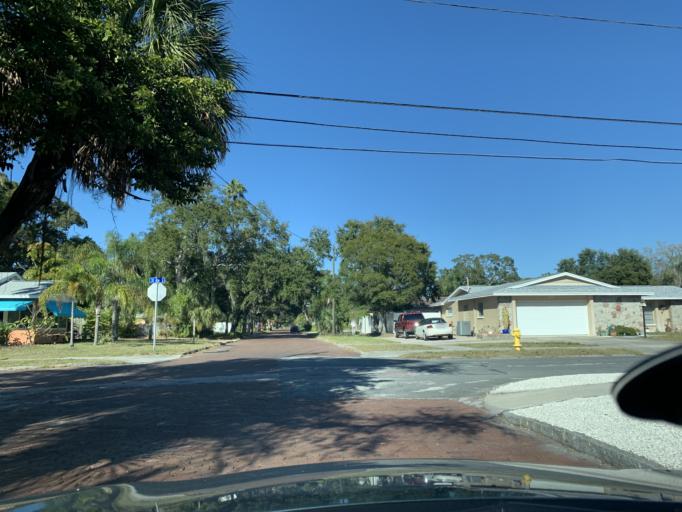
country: US
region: Florida
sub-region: Pinellas County
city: Gulfport
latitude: 27.7388
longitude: -82.7052
